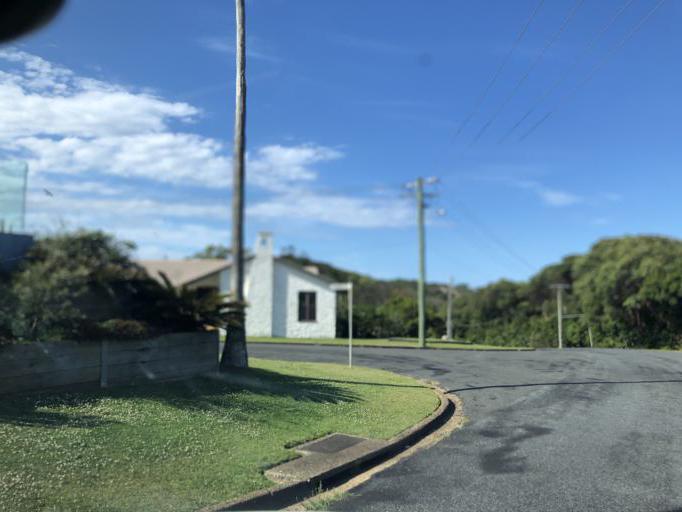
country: AU
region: New South Wales
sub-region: Coffs Harbour
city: Moonee Beach
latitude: -30.2376
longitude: 153.1502
